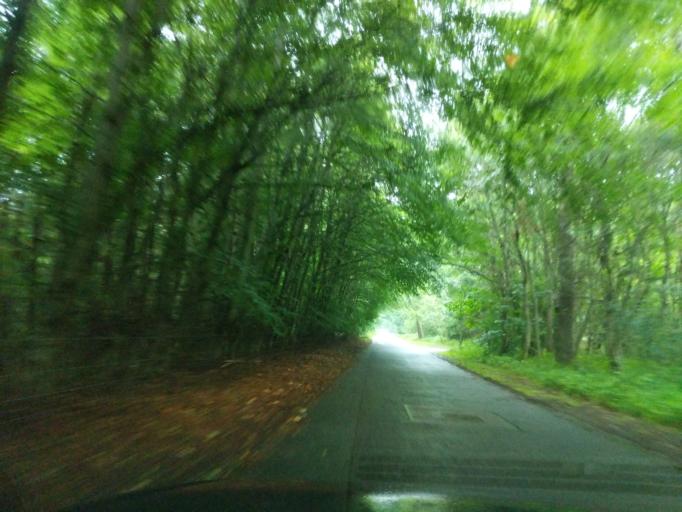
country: GB
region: Scotland
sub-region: Aberdeenshire
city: Aboyne
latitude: 57.0747
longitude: -2.8039
